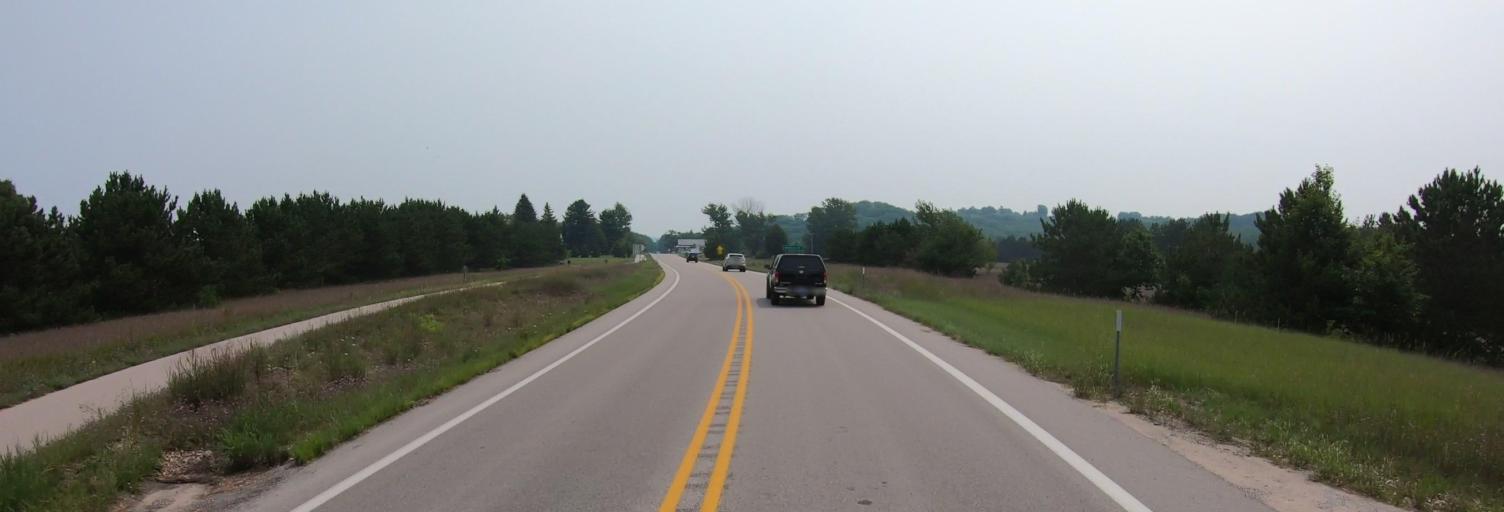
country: US
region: Michigan
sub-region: Leelanau County
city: Leland
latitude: 44.9219
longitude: -85.8766
